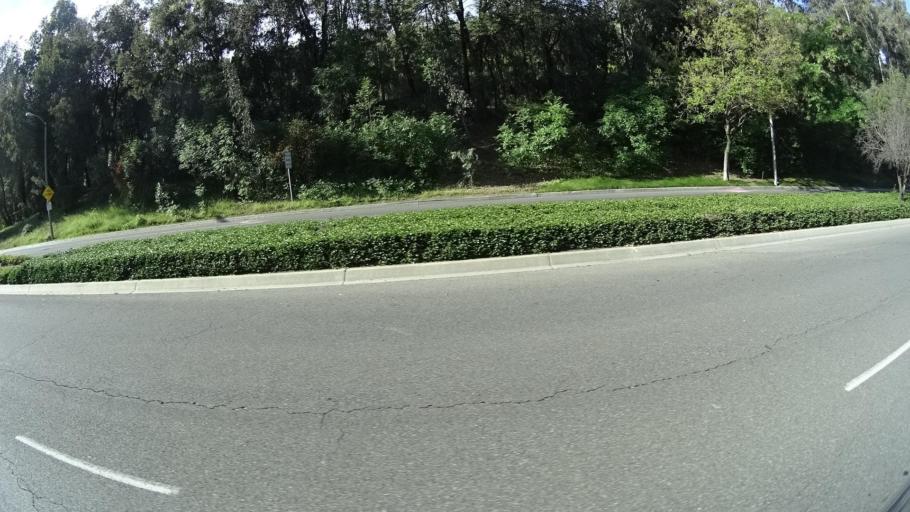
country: US
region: California
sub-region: Los Angeles County
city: Avocado Heights
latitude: 34.0282
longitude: -118.0173
